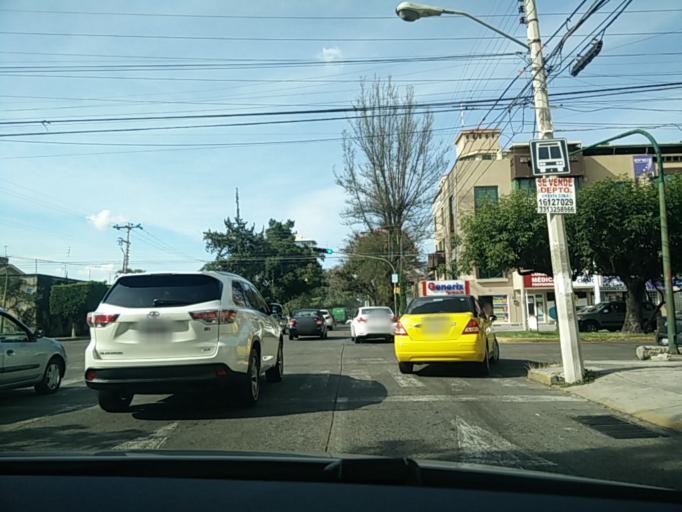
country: MX
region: Jalisco
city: Guadalajara
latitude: 20.6872
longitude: -103.3869
